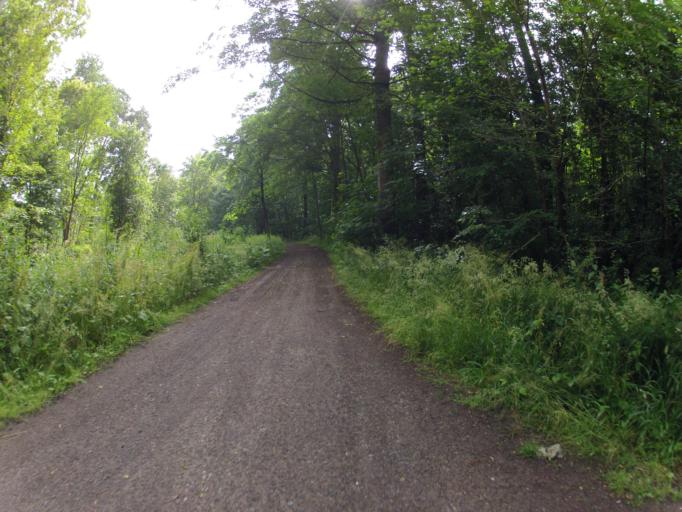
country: DE
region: Saxony
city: Markkleeberg
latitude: 51.3000
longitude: 12.3493
